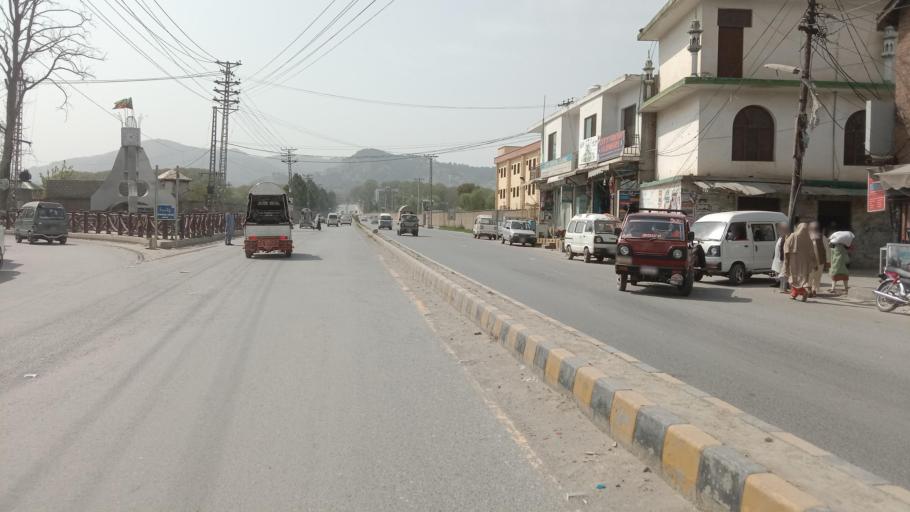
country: PK
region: Khyber Pakhtunkhwa
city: Abbottabad
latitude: 34.1569
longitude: 73.2328
